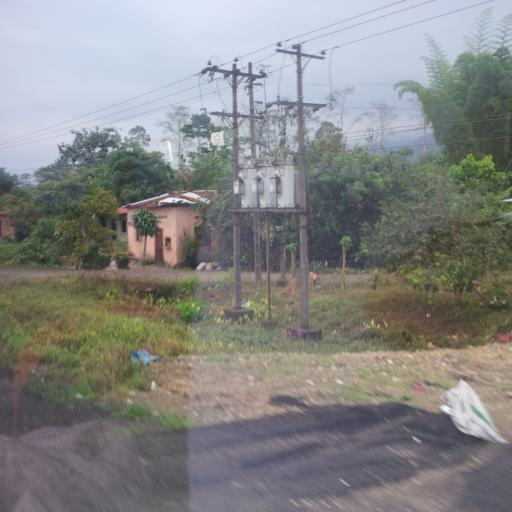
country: EC
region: Canar
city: La Troncal
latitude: -2.2523
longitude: -79.2066
